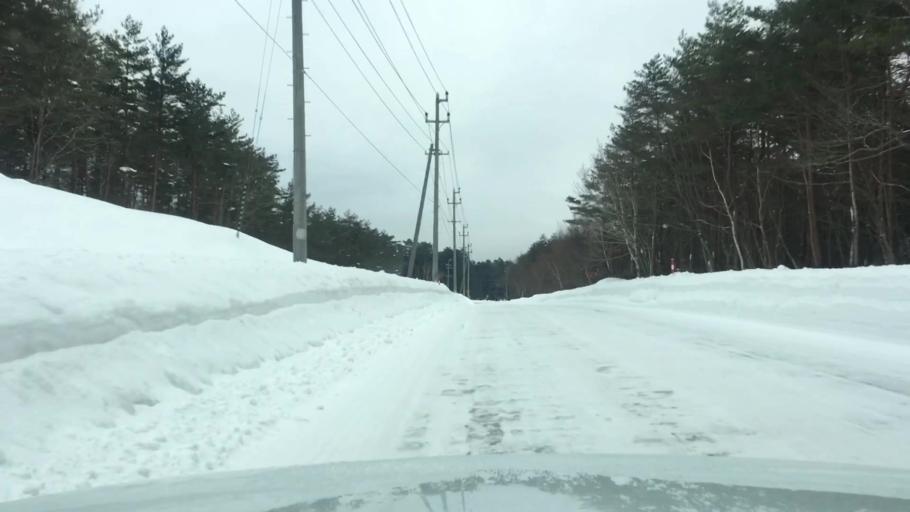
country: JP
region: Iwate
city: Shizukuishi
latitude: 39.9809
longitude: 141.0020
